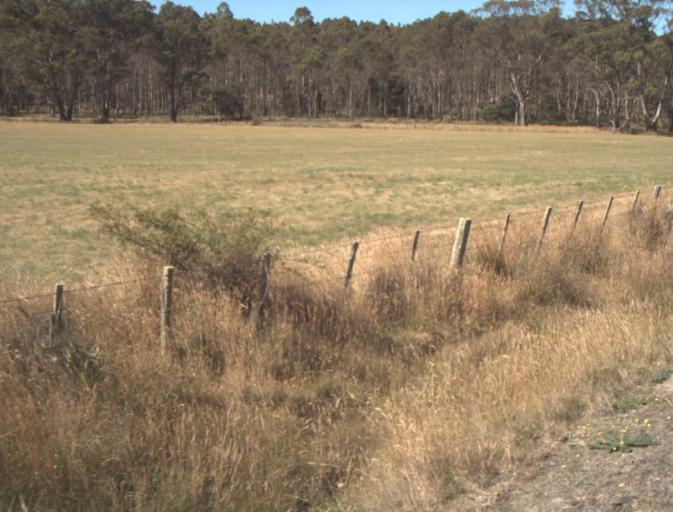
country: AU
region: Tasmania
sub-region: Launceston
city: Newstead
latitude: -41.3239
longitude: 147.3196
